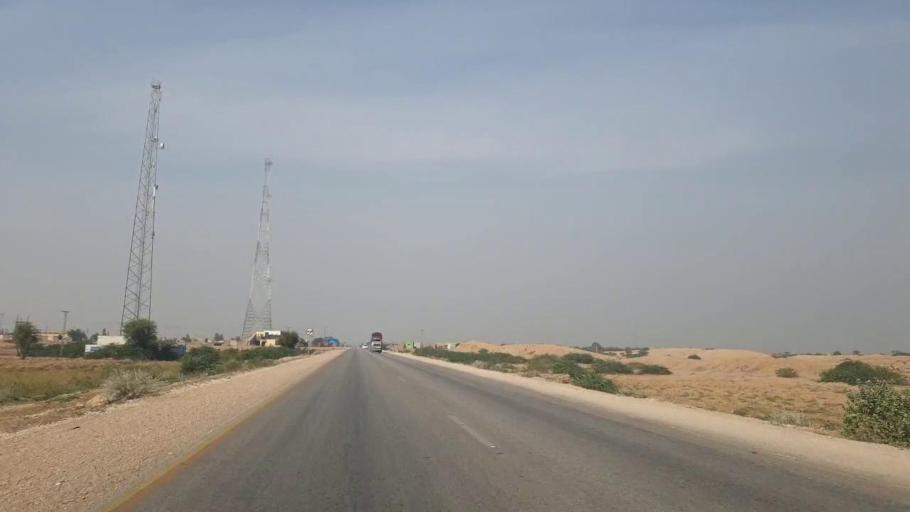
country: PK
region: Sindh
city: Sann
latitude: 26.0526
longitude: 68.1074
